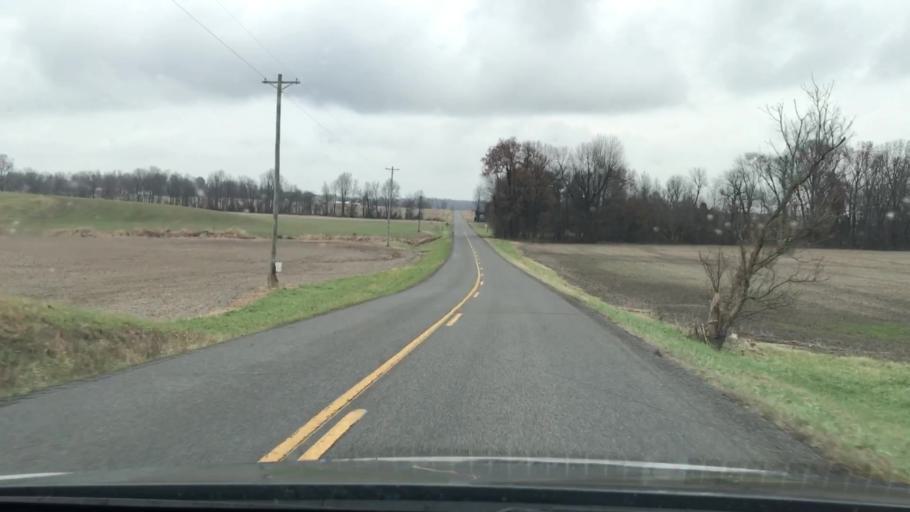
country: US
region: Kentucky
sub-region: Webster County
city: Sebree
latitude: 37.5003
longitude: -87.4360
